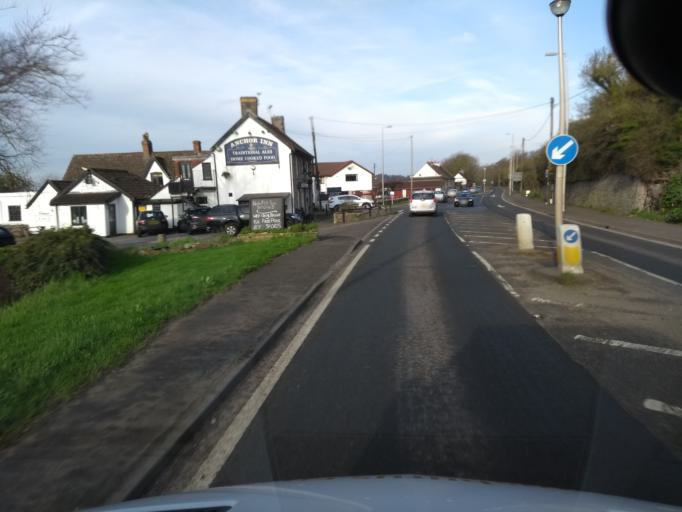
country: GB
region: England
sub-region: North Somerset
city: Bleadon
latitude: 51.3083
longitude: -2.9594
